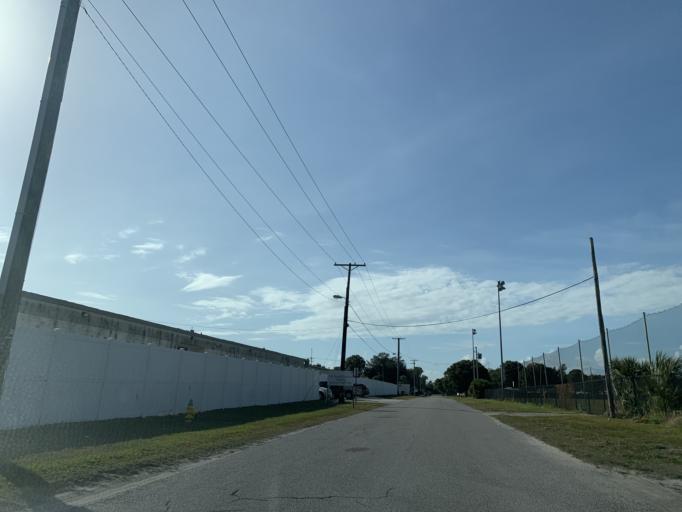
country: US
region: Florida
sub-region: Hillsborough County
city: Tampa
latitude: 27.8974
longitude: -82.5085
